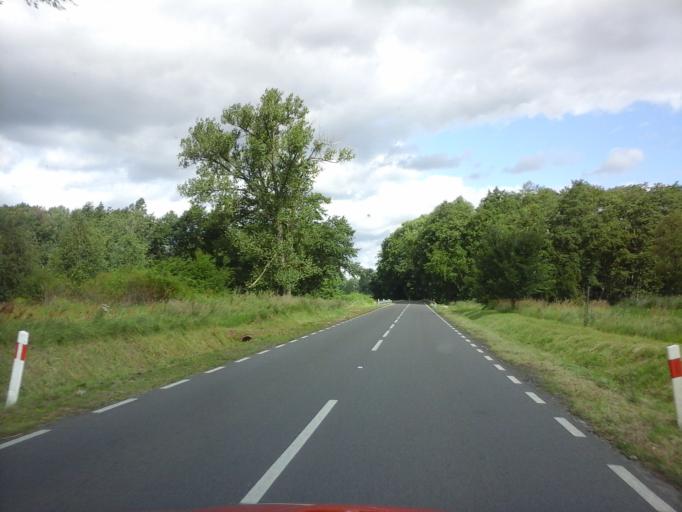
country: PL
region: West Pomeranian Voivodeship
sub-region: Powiat stargardzki
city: Kobylanka
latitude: 53.3434
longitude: 14.9415
